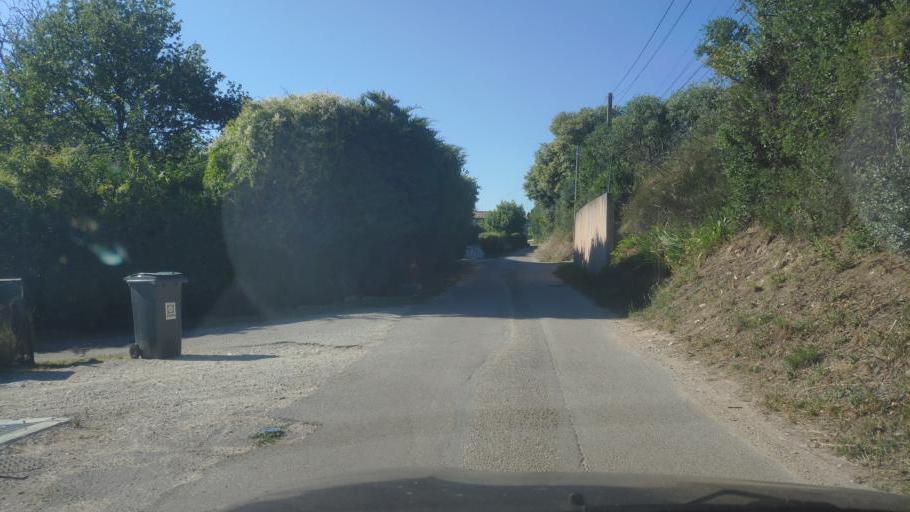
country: FR
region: Provence-Alpes-Cote d'Azur
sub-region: Departement du Vaucluse
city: Carpentras
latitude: 44.0703
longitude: 5.0500
